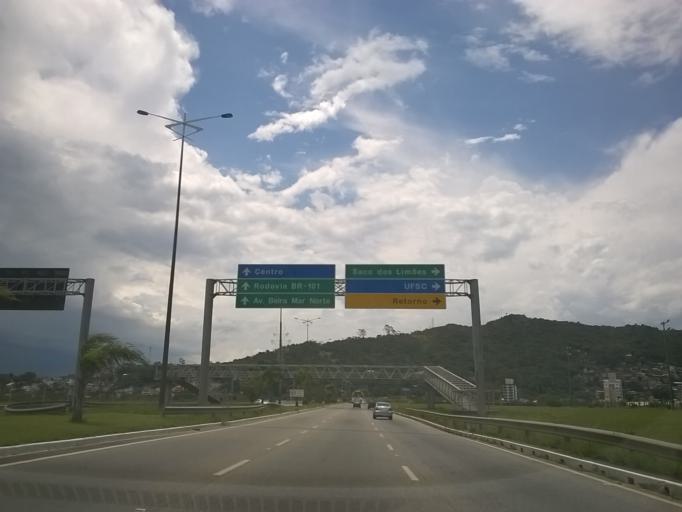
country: BR
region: Santa Catarina
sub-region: Florianopolis
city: Saco dos Limoes
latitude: -27.6128
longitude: -48.5324
